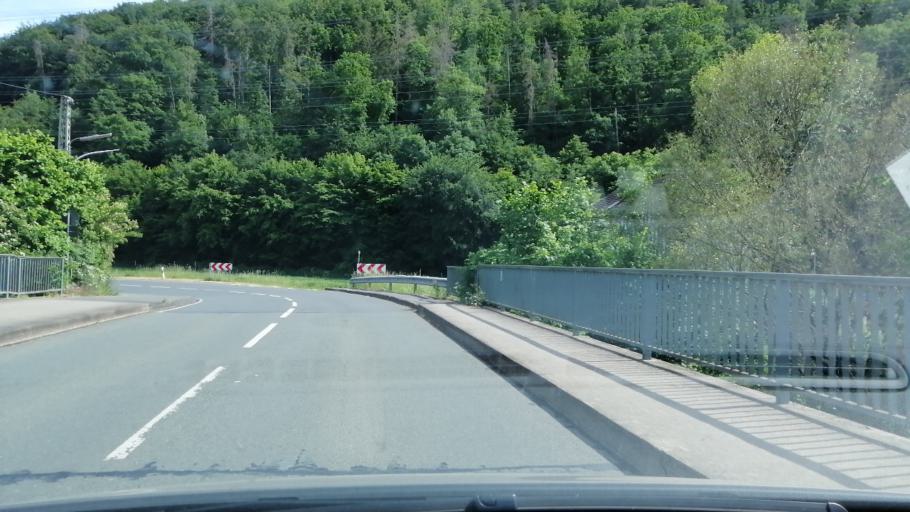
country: DE
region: Hesse
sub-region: Regierungsbezirk Kassel
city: Waldeck
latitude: 51.1649
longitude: 9.0873
